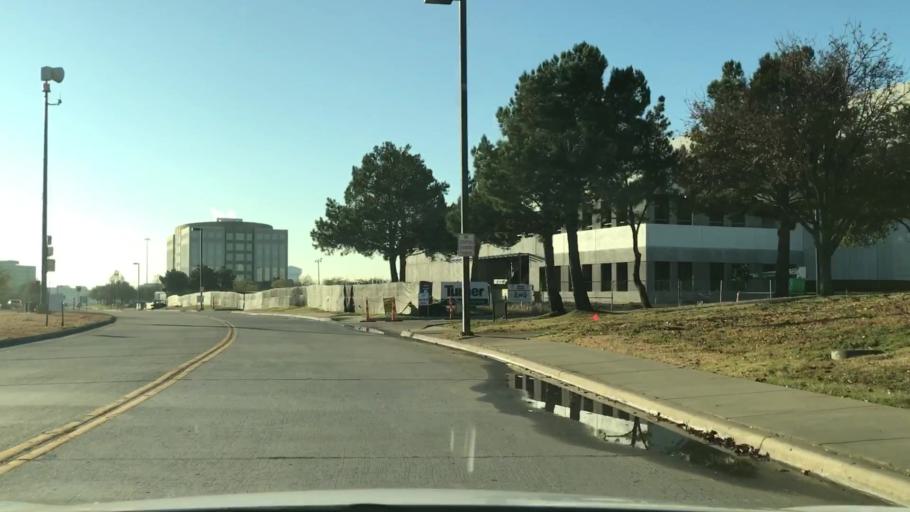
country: US
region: Texas
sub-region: Dallas County
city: Coppell
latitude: 32.8962
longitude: -96.9813
